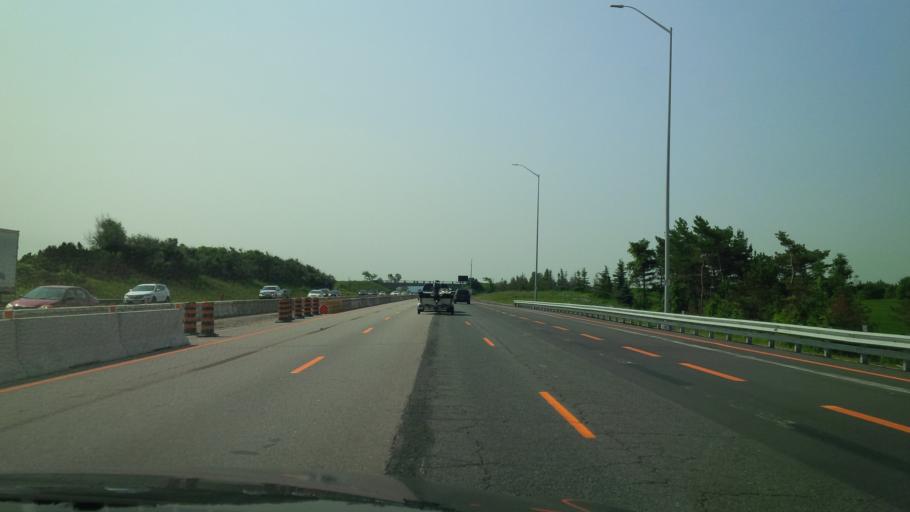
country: CA
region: Ontario
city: Innisfil
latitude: 44.2406
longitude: -79.6679
